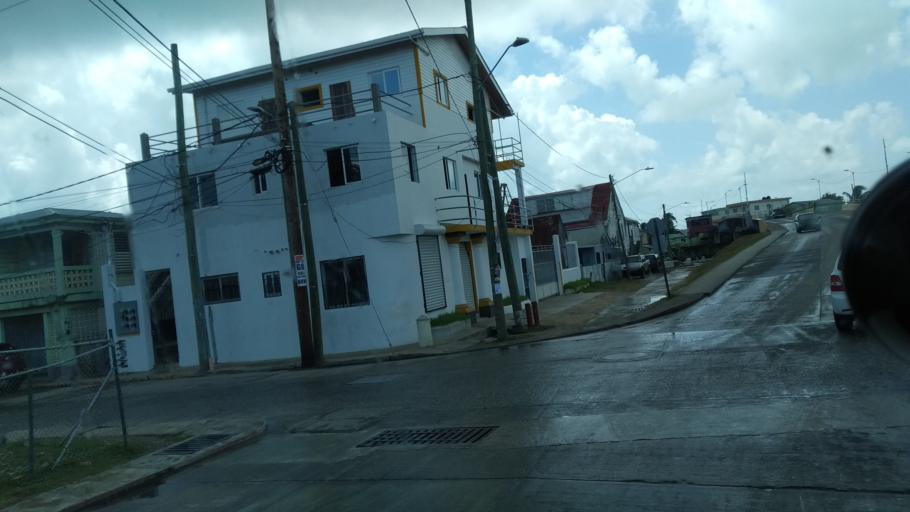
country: BZ
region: Belize
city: Belize City
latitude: 17.5000
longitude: -88.1917
